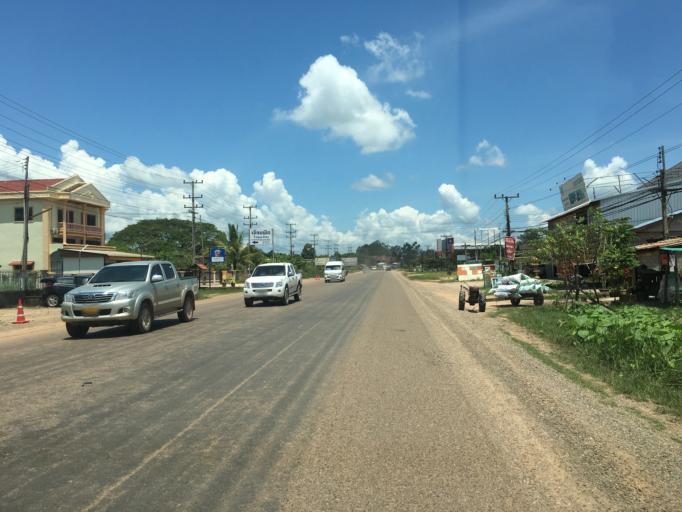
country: LA
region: Vientiane
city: Vientiane
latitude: 18.0554
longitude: 102.5415
